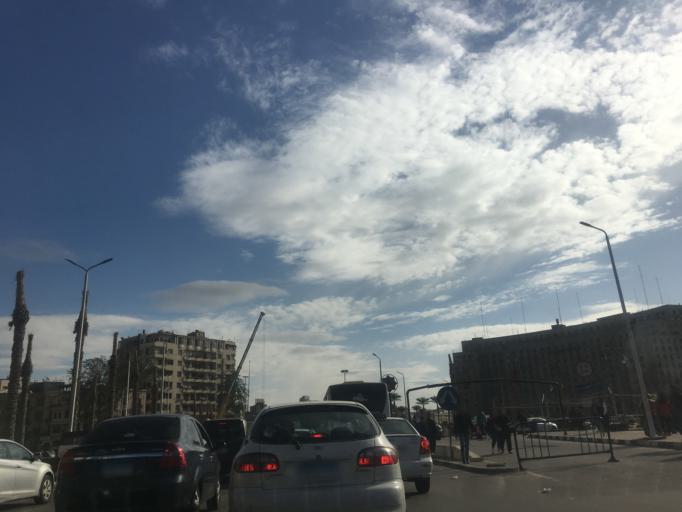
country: EG
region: Muhafazat al Qahirah
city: Cairo
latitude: 30.0457
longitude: 31.2350
